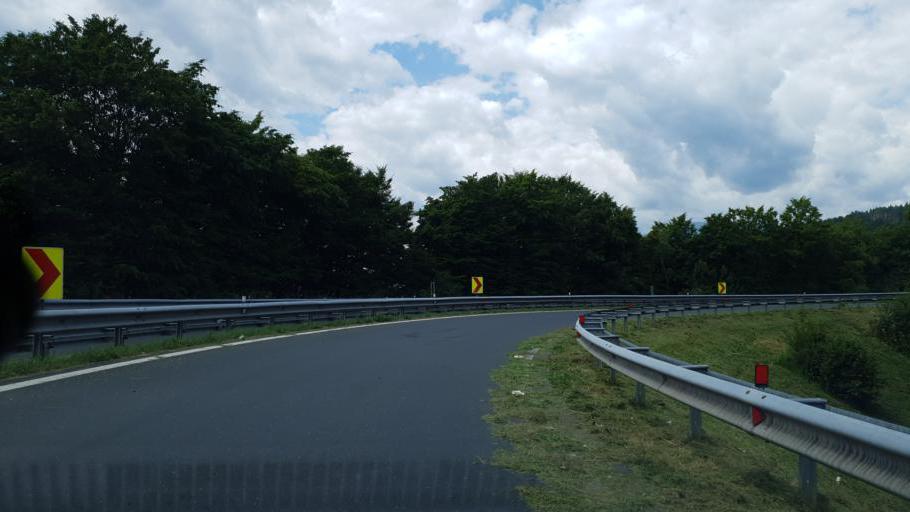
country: AT
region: Carinthia
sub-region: Politischer Bezirk Spittal an der Drau
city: Spittal an der Drau
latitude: 46.7782
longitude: 13.5384
